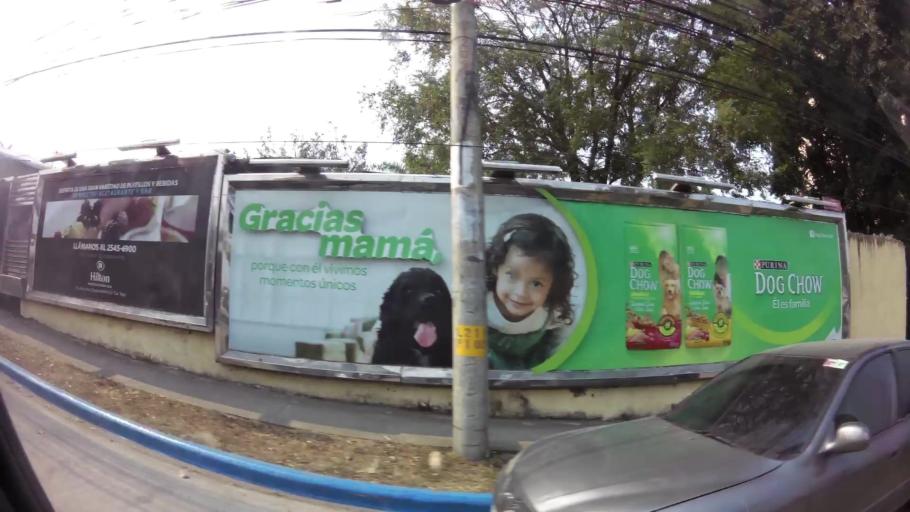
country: HN
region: Cortes
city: Armenta
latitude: 15.4987
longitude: -88.0384
